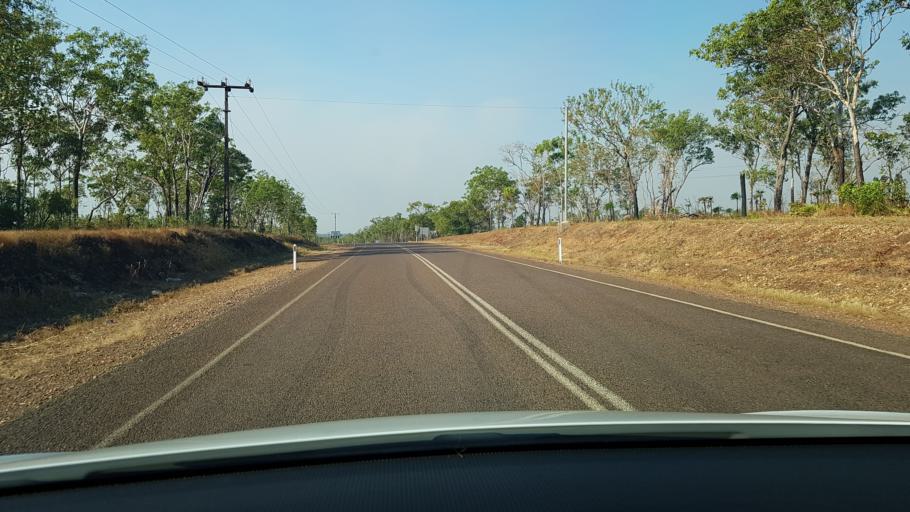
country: AU
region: Northern Territory
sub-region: Litchfield
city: McMinns Lagoon
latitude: -12.6995
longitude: 131.0167
